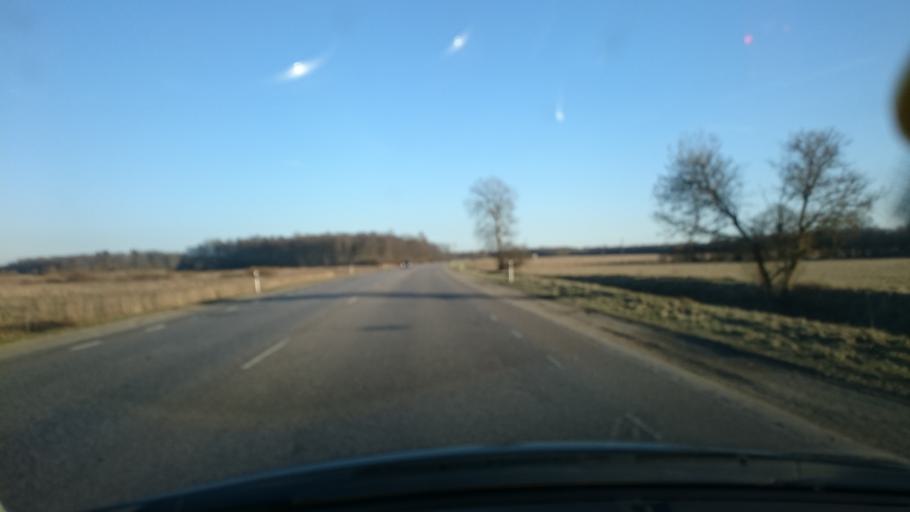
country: EE
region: Harju
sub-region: Rae vald
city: Jueri
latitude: 59.3902
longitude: 24.9197
